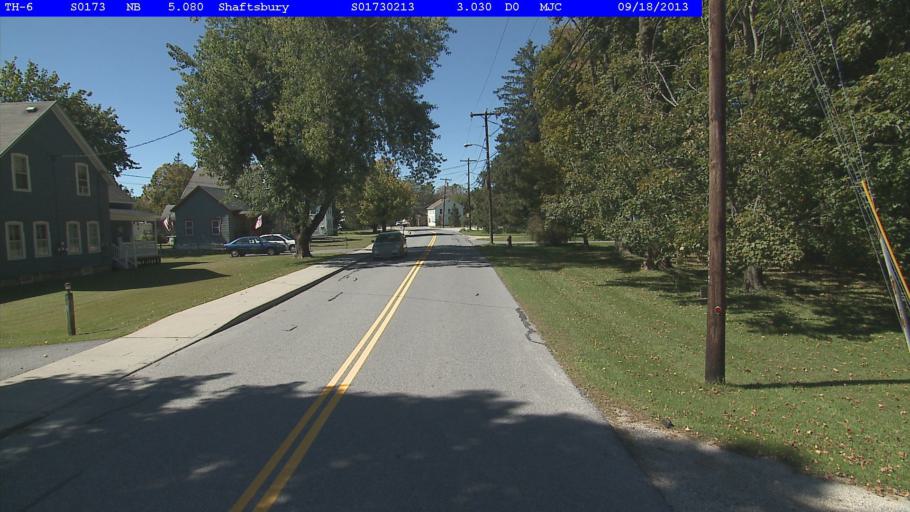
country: US
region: Vermont
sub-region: Bennington County
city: North Bennington
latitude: 42.9461
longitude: -73.2083
